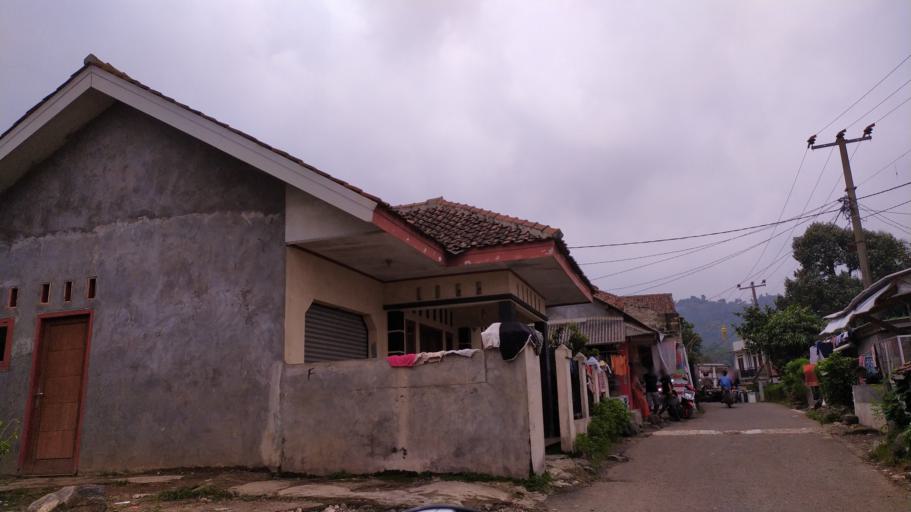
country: ID
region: West Java
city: Ciampea
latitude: -6.6159
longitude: 106.7088
